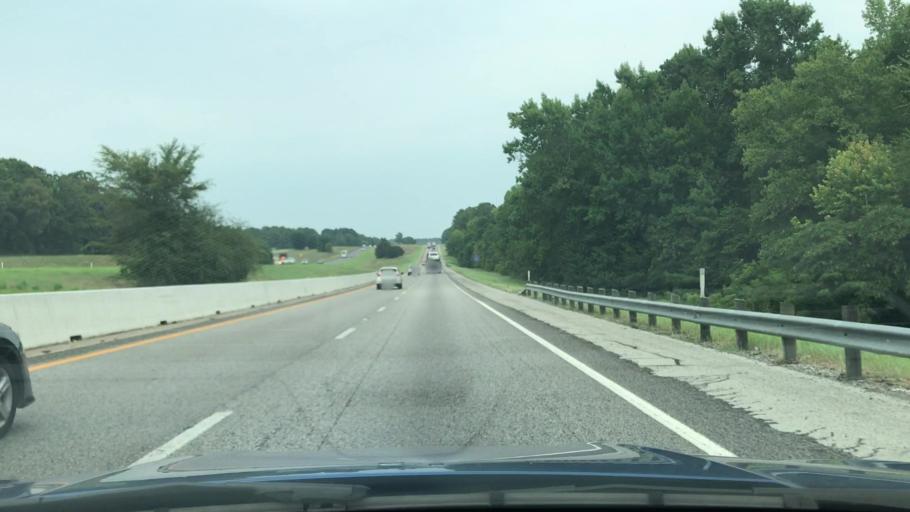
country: US
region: Texas
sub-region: Smith County
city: Lindale
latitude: 32.4682
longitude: -95.3625
